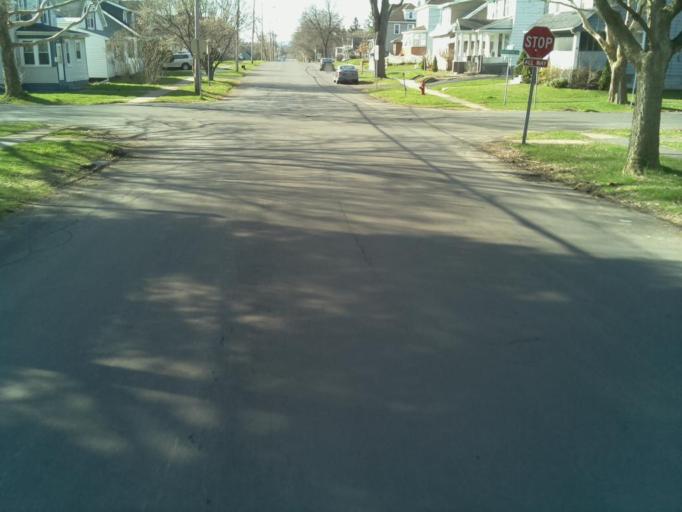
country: US
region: New York
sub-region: Onondaga County
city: Lyncourt
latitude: 43.0653
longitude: -76.1123
